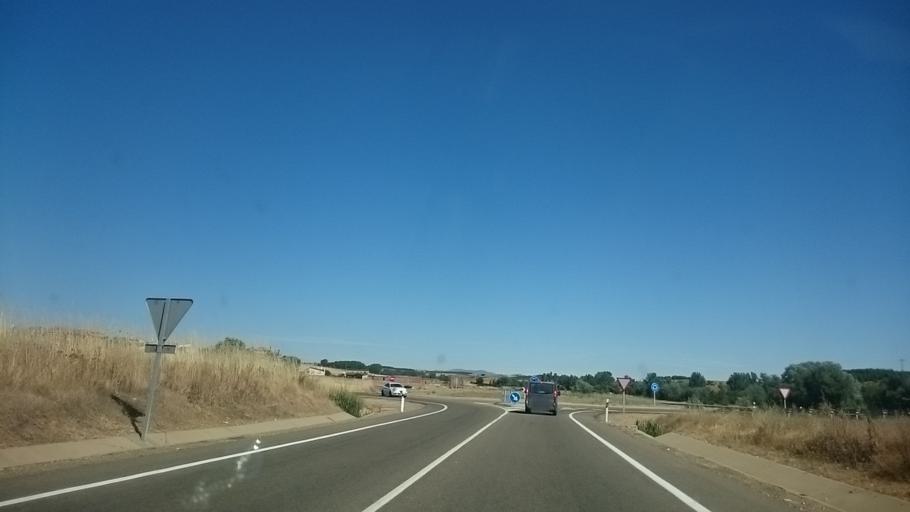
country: ES
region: Castille and Leon
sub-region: Provincia de Leon
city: Valdefresno
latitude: 42.5637
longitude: -5.4894
